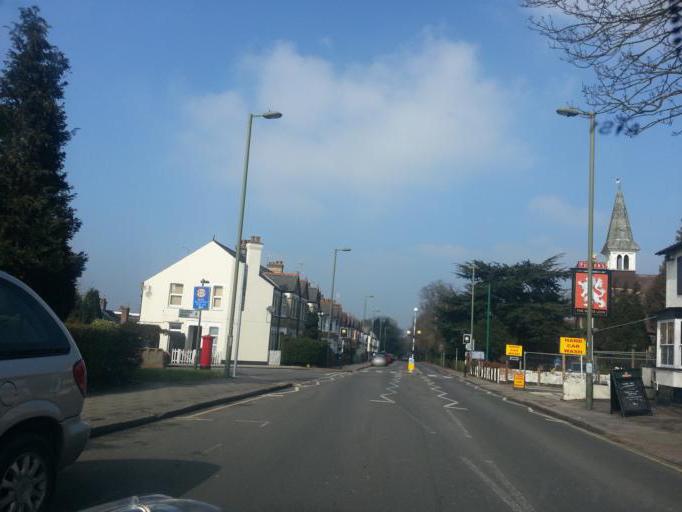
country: GB
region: England
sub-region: Greater London
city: High Barnet
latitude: 51.6579
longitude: -0.2043
